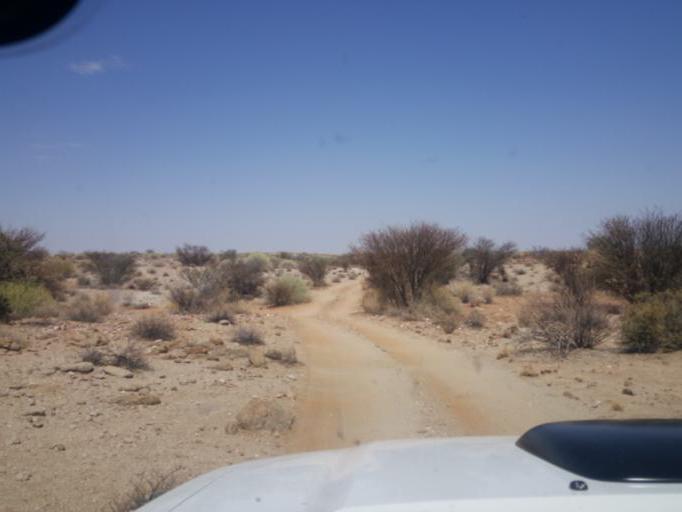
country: ZA
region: Northern Cape
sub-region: Siyanda District Municipality
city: Kakamas
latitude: -28.5888
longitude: 20.2651
